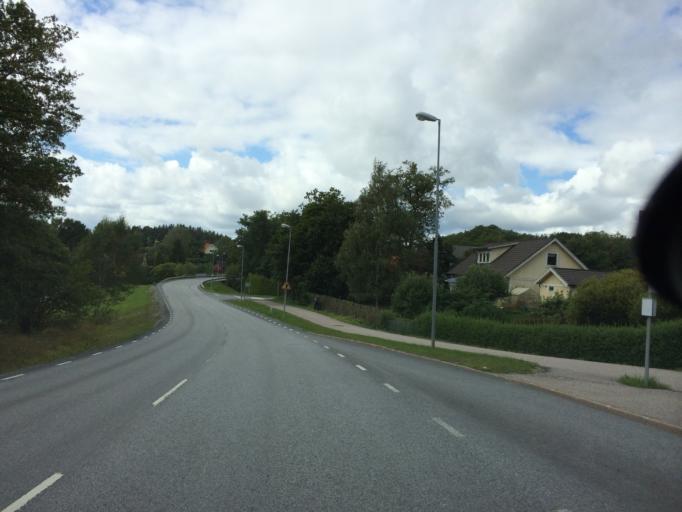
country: SE
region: Stockholm
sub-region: Sollentuna Kommun
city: Sollentuna
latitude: 59.4585
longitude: 17.9056
